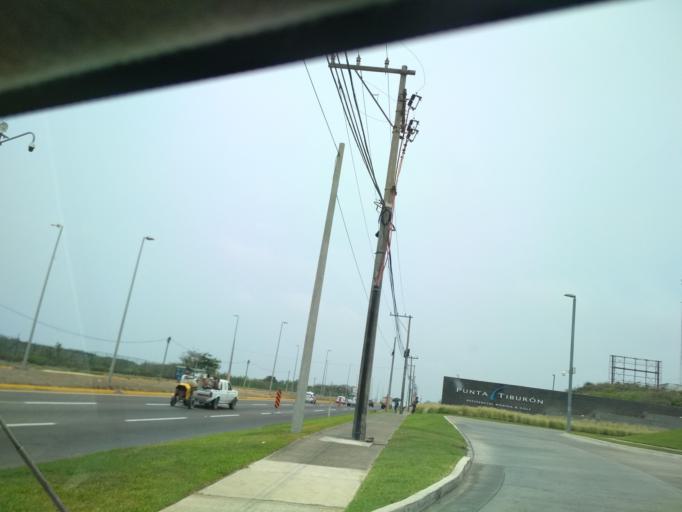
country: MX
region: Veracruz
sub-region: Alvarado
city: Playa de la Libertad
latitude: 19.0680
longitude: -96.0817
